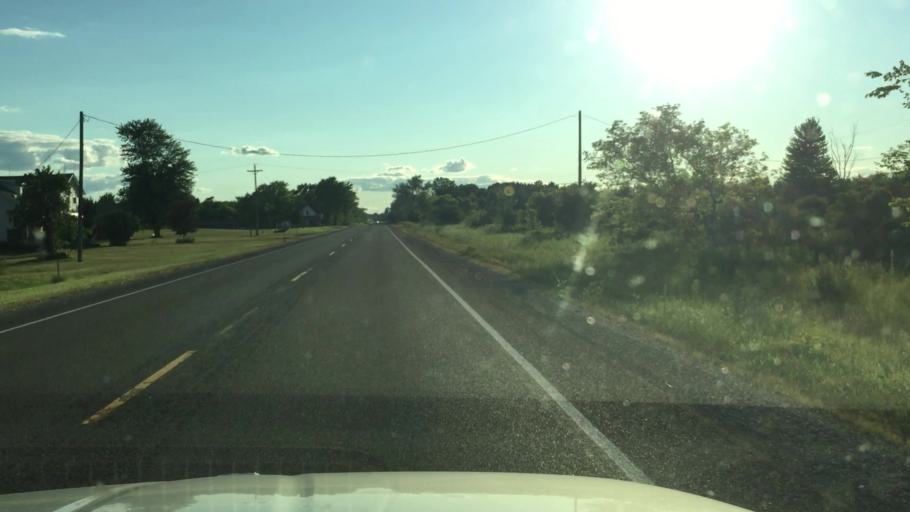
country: US
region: Michigan
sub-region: Saint Clair County
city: Capac
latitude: 43.0263
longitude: -82.9769
